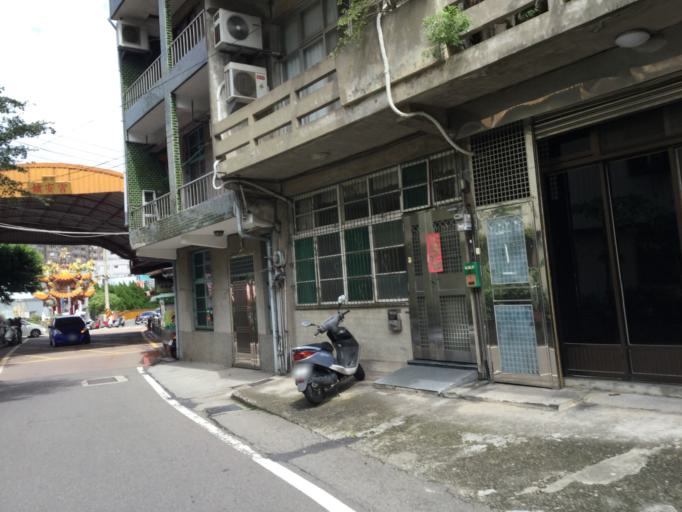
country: TW
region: Taiwan
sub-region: Hsinchu
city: Hsinchu
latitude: 24.7832
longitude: 121.0134
